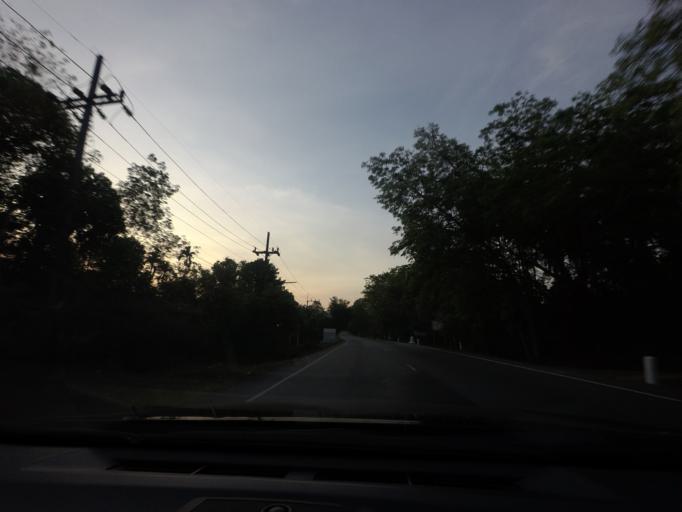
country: TH
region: Narathiwat
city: Rueso
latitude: 6.3618
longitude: 101.6096
